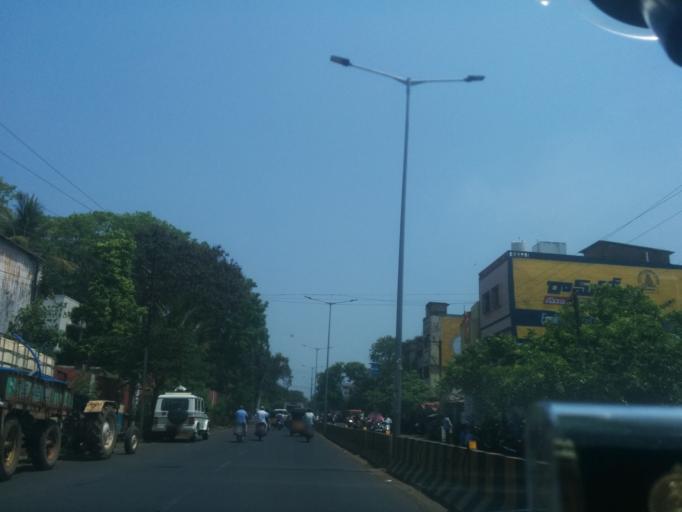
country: IN
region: Andhra Pradesh
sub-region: East Godavari
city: Rajahmundry
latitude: 17.0226
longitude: 81.7749
